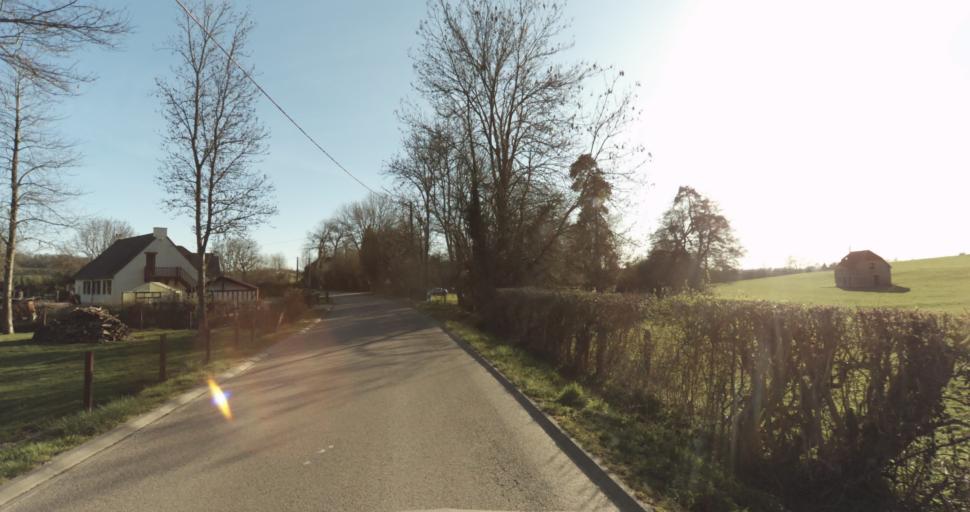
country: FR
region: Lower Normandy
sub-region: Departement du Calvados
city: Saint-Pierre-sur-Dives
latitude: 48.9626
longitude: 0.0515
